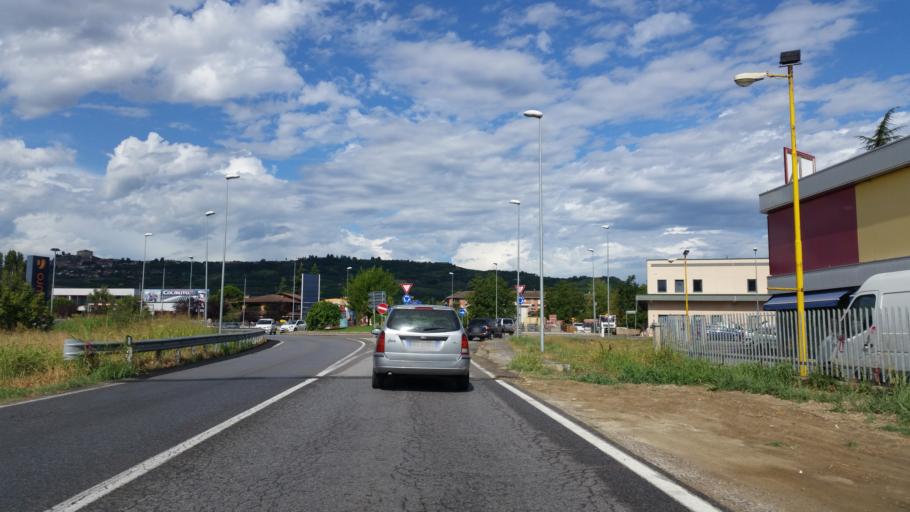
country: IT
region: Piedmont
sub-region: Provincia di Cuneo
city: Sant'Antonio
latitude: 44.7444
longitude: 8.0681
